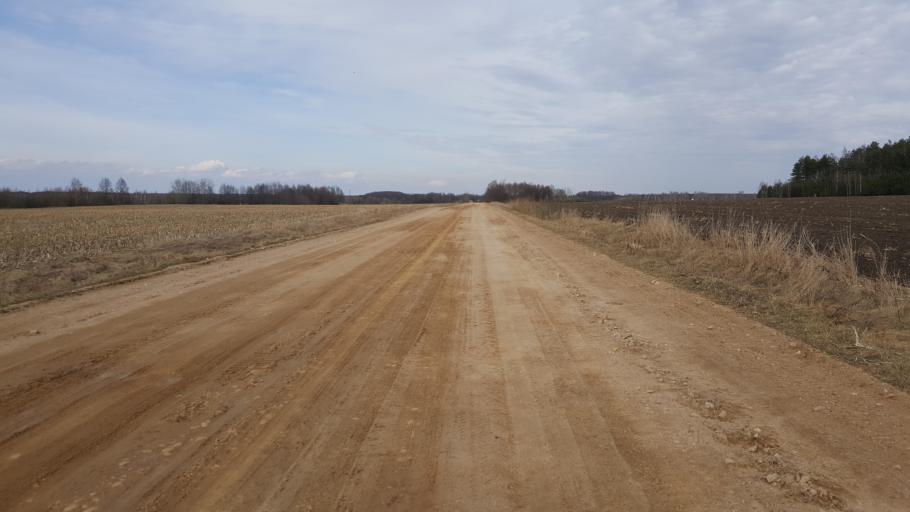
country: BY
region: Brest
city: Zhabinka
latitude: 52.3816
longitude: 23.9934
